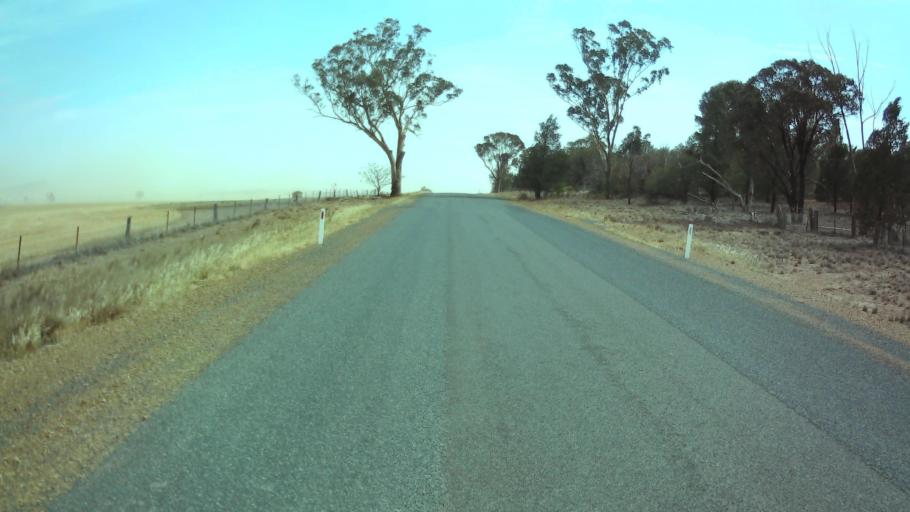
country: AU
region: New South Wales
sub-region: Weddin
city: Grenfell
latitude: -33.7472
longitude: 147.9915
